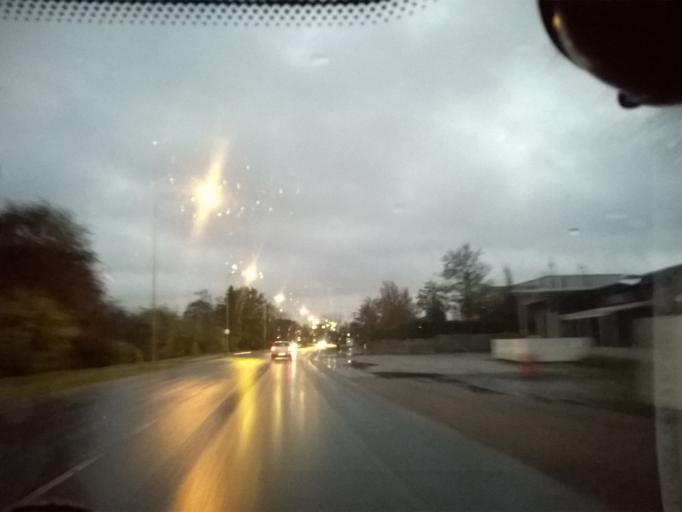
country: EE
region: Harju
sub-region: Viimsi vald
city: Rummu
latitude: 59.5278
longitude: 24.7973
